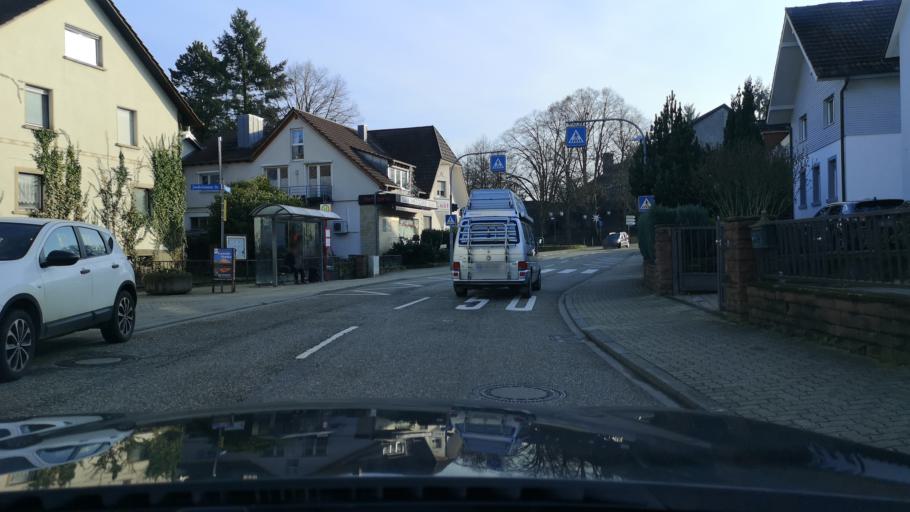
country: DE
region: Baden-Wuerttemberg
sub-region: Karlsruhe Region
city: Ettlingen
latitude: 48.9685
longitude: 8.4781
